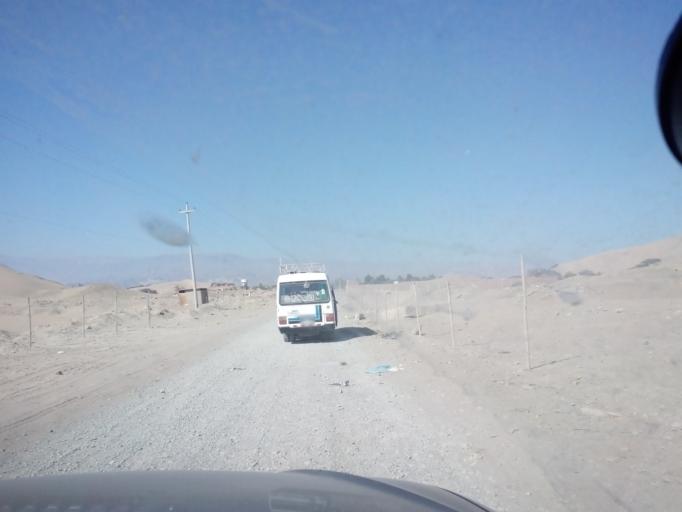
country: PE
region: Ica
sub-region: Provincia de Ica
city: Ica
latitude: -14.0778
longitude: -75.7632
